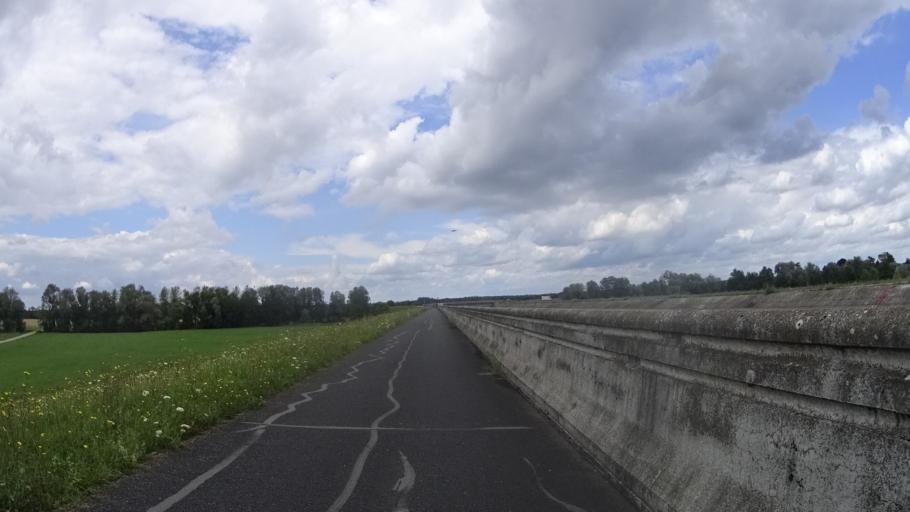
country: FR
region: Champagne-Ardenne
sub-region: Departement de la Haute-Marne
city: Villiers-en-Lieu
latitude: 48.5895
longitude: 4.8568
